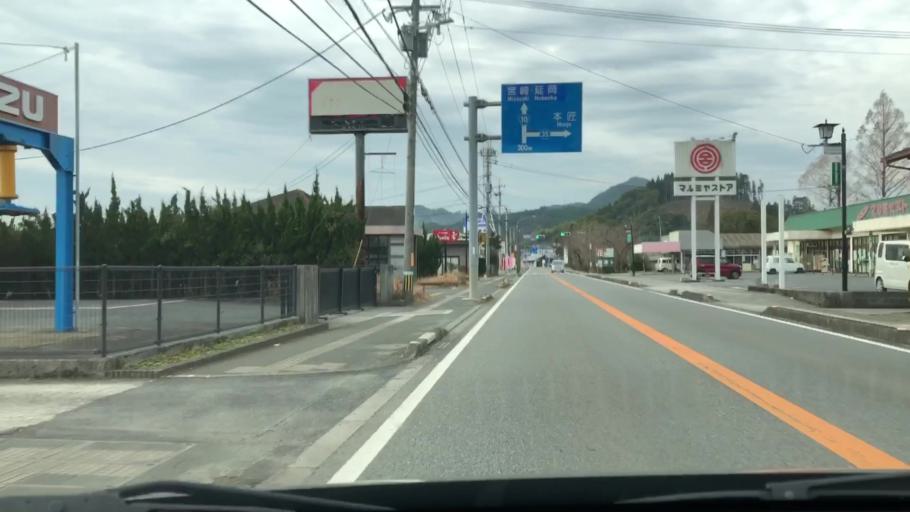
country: JP
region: Oita
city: Saiki
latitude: 32.9716
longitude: 131.8407
